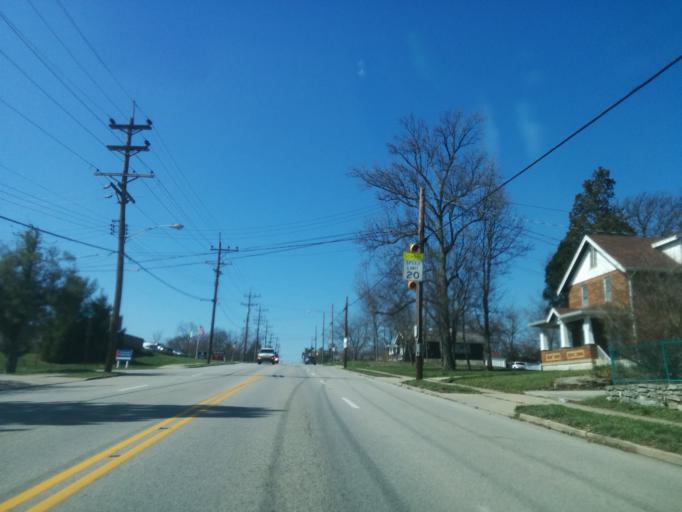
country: US
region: Ohio
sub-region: Hamilton County
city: Monfort Heights
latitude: 39.1896
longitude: -84.5848
